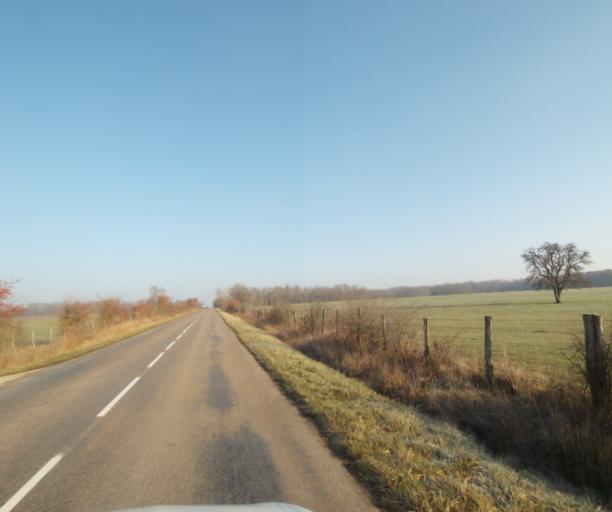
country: FR
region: Champagne-Ardenne
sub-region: Departement de la Haute-Marne
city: Montier-en-Der
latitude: 48.4241
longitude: 4.7475
